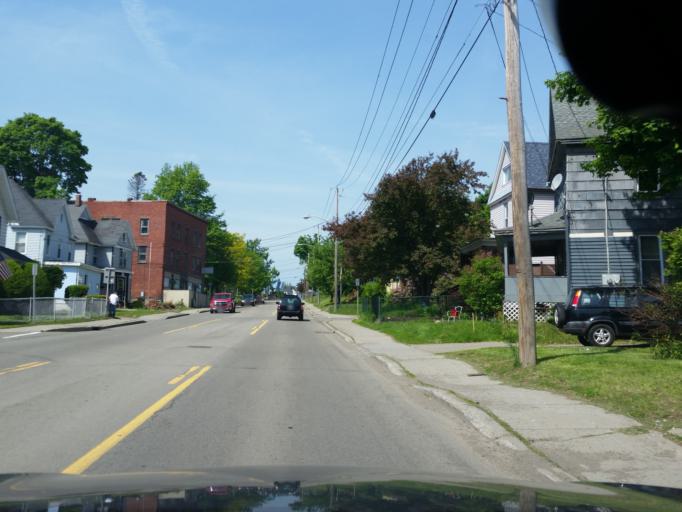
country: US
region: New York
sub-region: Chautauqua County
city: Jamestown
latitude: 42.0980
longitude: -79.2583
